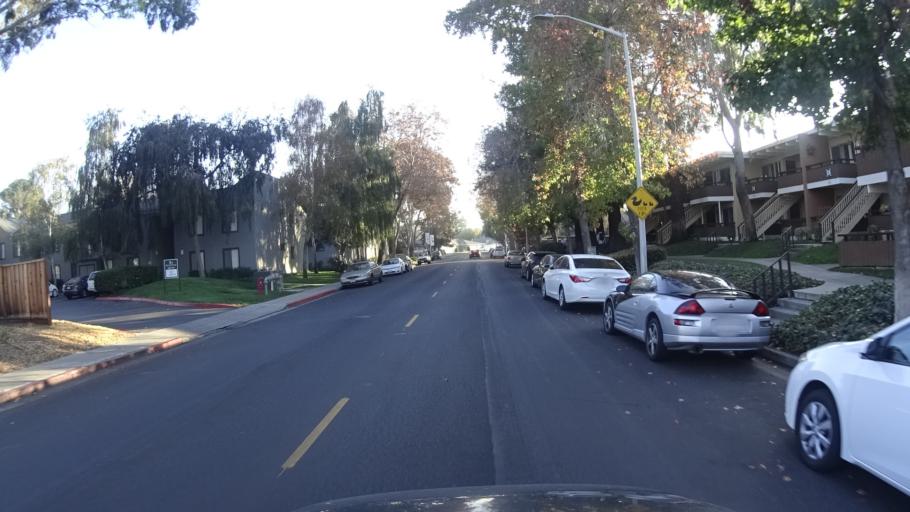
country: US
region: California
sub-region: Santa Clara County
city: Santa Clara
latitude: 37.3479
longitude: -121.9932
